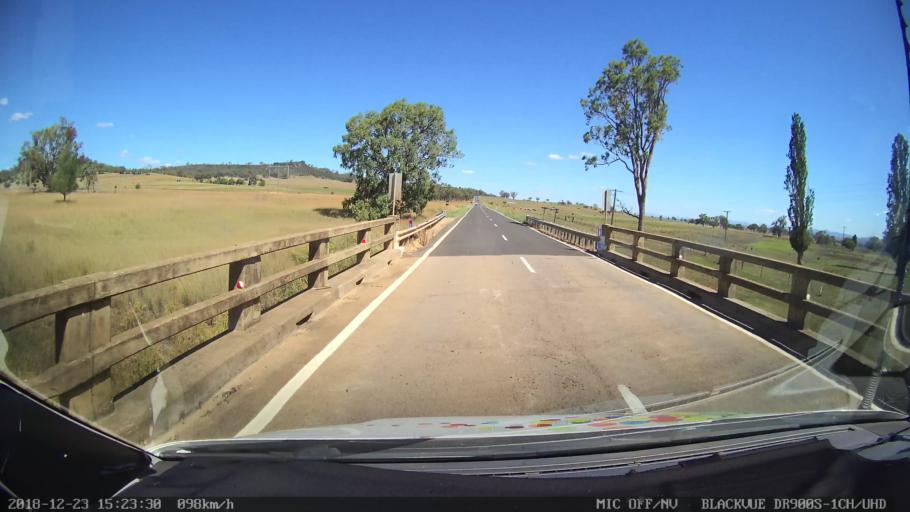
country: AU
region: New South Wales
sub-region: Tamworth Municipality
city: Manilla
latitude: -30.8810
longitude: 150.8147
